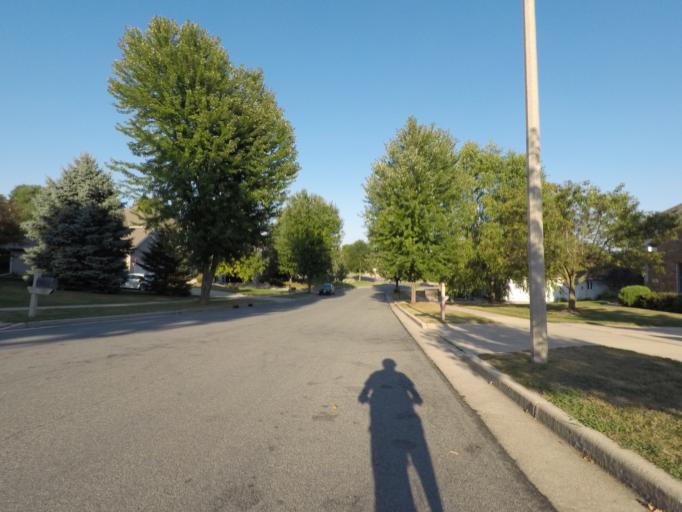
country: US
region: Wisconsin
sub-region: Dane County
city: Verona
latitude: 43.0054
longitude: -89.5368
